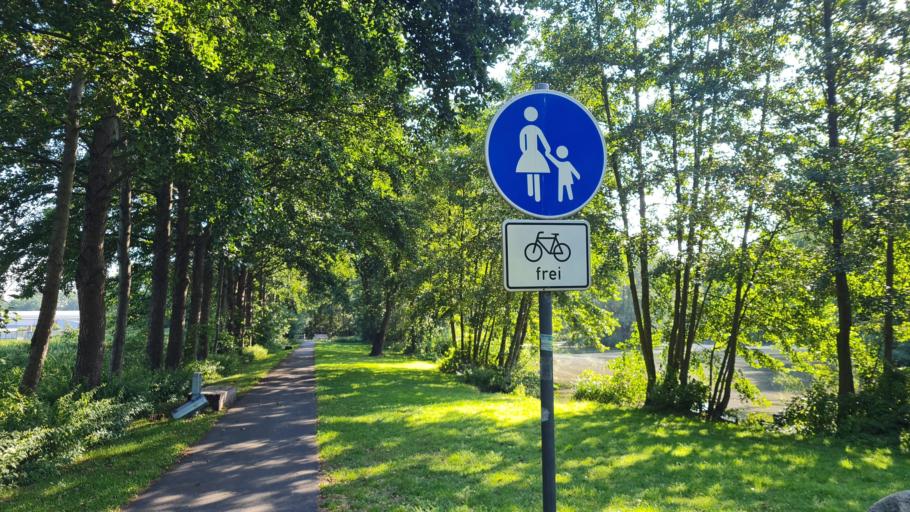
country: DE
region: Lower Saxony
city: Dahlenburg
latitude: 53.1817
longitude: 10.7448
